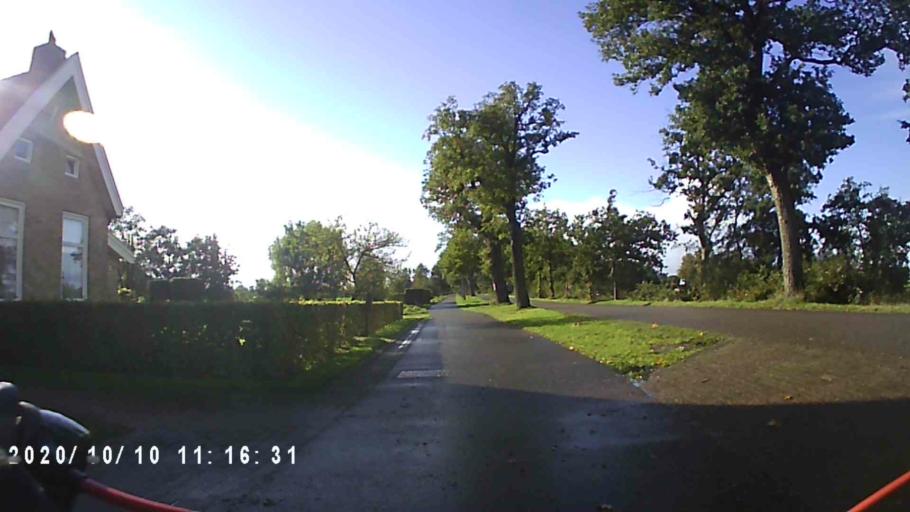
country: NL
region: Friesland
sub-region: Gemeente Smallingerland
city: Drachtstercompagnie
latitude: 53.0994
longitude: 6.1996
